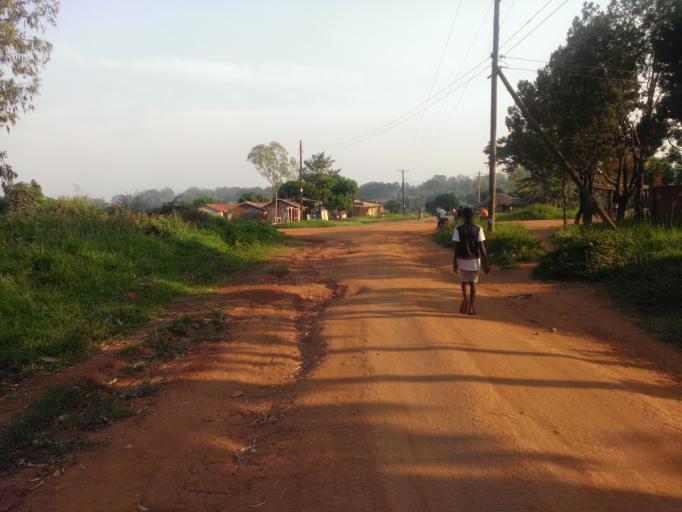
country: UG
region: Northern Region
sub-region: Gulu District
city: Gulu
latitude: 2.7793
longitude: 32.3037
